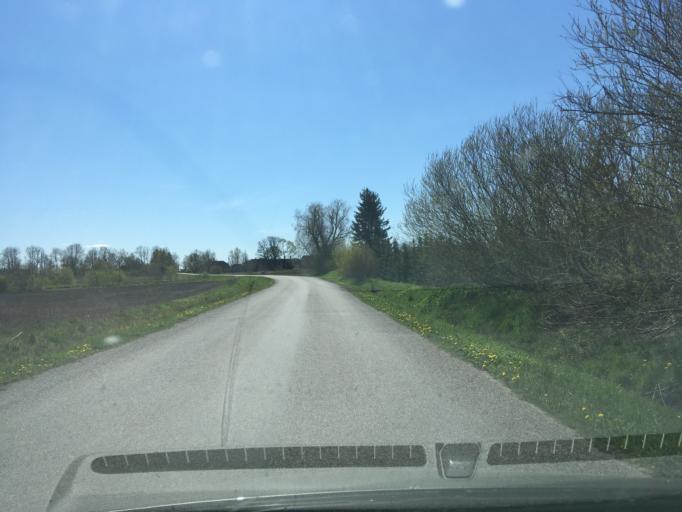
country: EE
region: Harju
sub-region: Raasiku vald
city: Arukula
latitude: 59.3946
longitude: 25.0793
